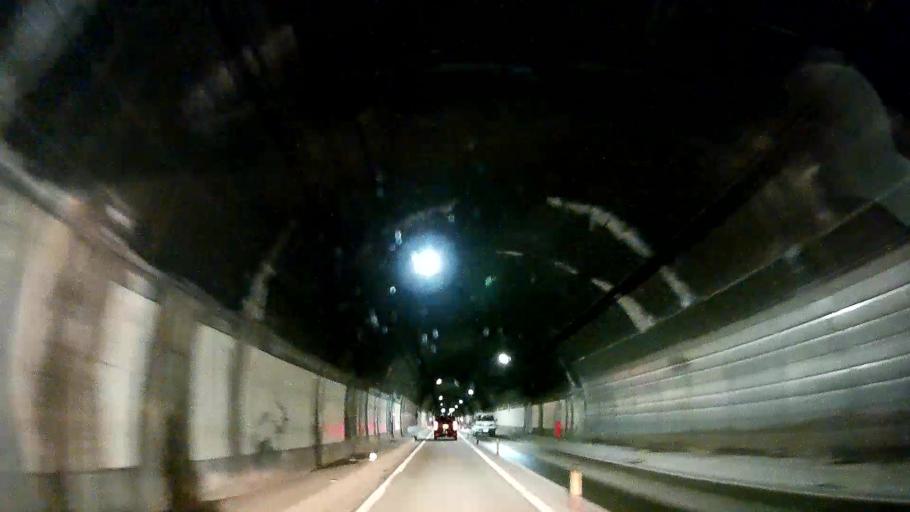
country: JP
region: Saitama
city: Chichibu
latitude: 35.9542
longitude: 139.1718
